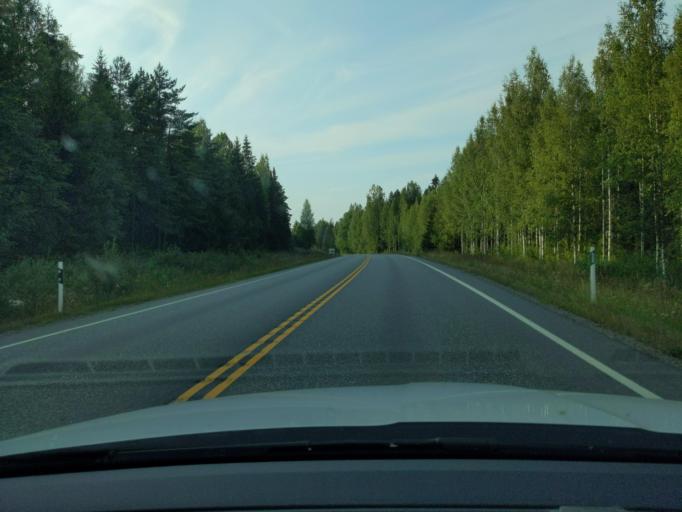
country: FI
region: Paijanne Tavastia
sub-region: Lahti
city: Padasjoki
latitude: 61.3332
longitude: 25.2684
